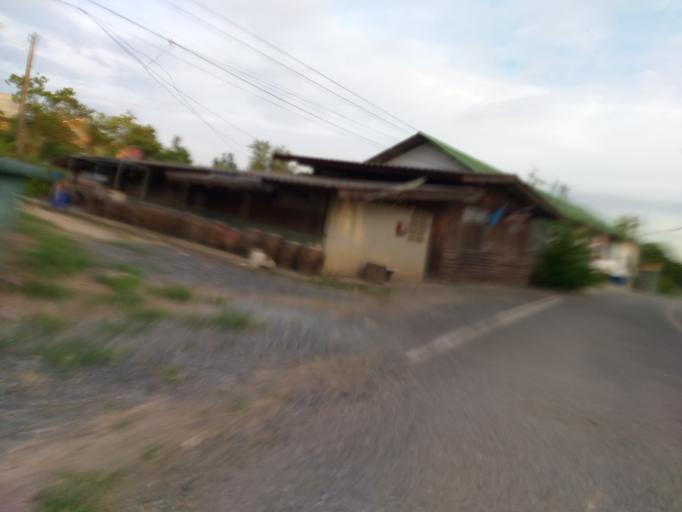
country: TH
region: Pathum Thani
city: Ban Lam Luk Ka
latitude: 13.9999
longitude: 100.7980
